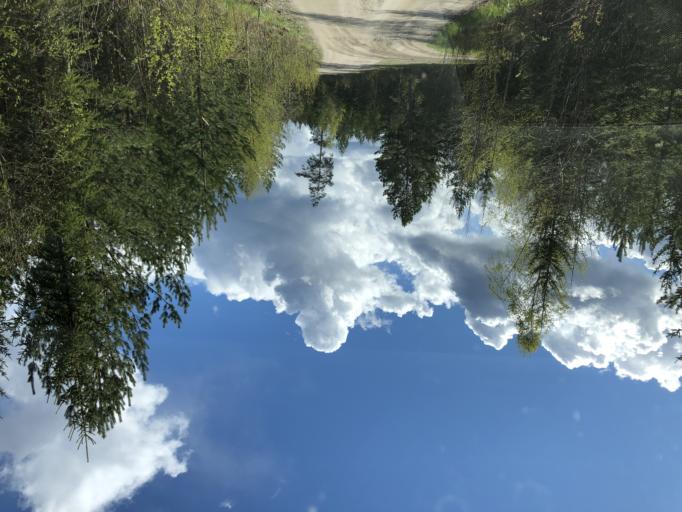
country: SE
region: Uppsala
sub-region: Heby Kommun
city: Tarnsjo
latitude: 60.2536
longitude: 16.9073
